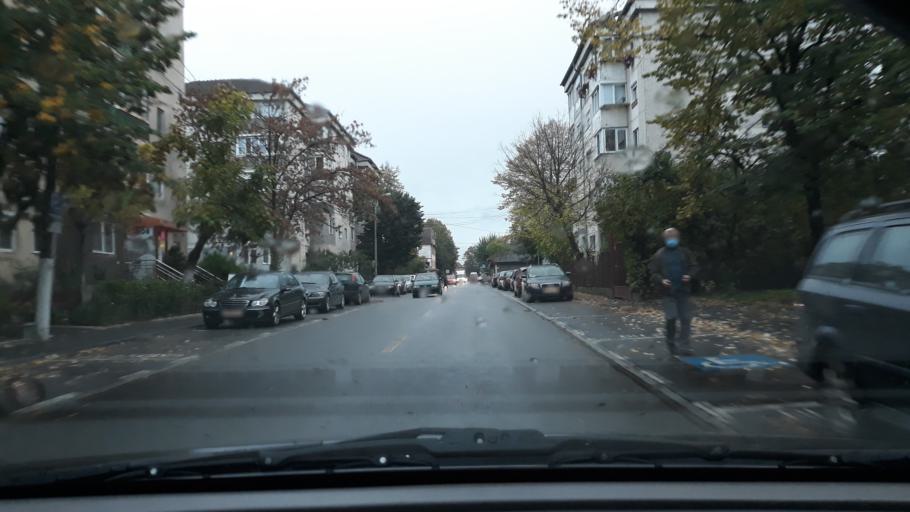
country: RO
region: Bihor
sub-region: Comuna Biharea
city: Oradea
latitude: 47.0338
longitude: 21.9460
